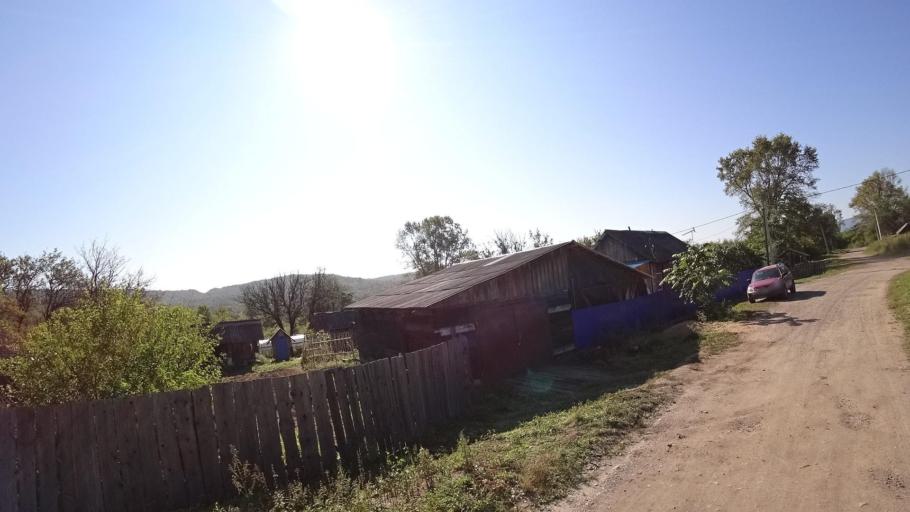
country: RU
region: Jewish Autonomous Oblast
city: Bira
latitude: 49.0043
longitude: 132.4732
